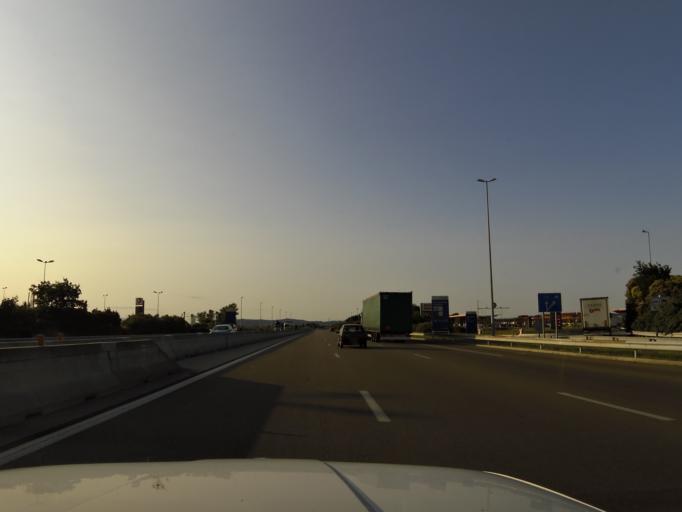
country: FR
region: Rhone-Alpes
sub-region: Departement de la Drome
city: La Roche-de-Glun
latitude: 45.0181
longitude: 4.8757
